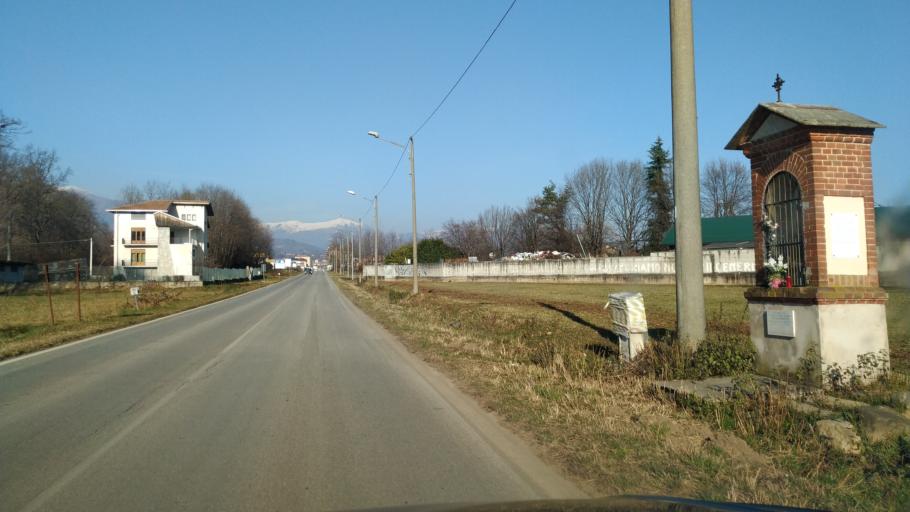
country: IT
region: Piedmont
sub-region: Provincia di Biella
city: Mongrando
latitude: 45.5353
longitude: 8.0114
